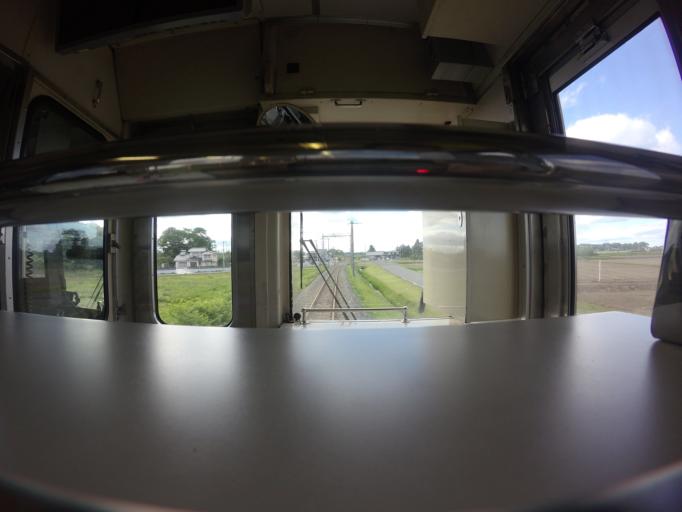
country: JP
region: Fukushima
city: Namie
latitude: 37.5954
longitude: 140.9981
